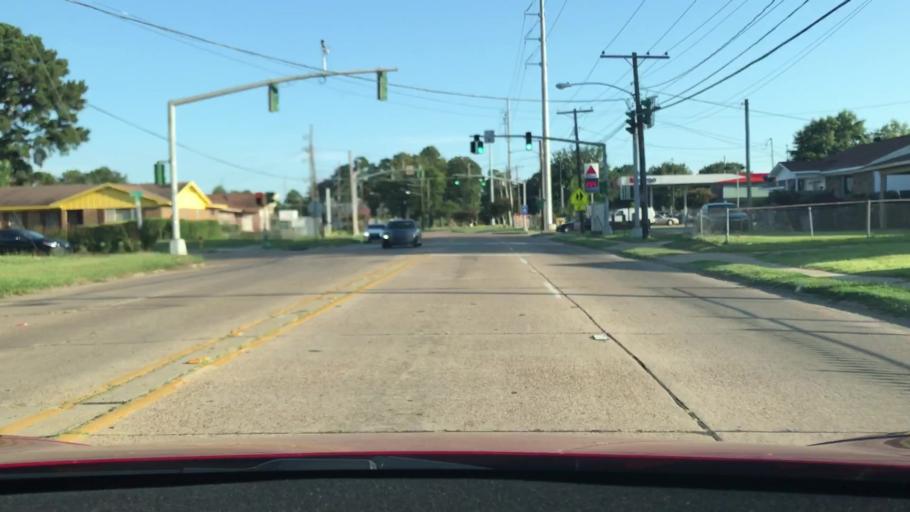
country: US
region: Louisiana
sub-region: Bossier Parish
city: Bossier City
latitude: 32.4336
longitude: -93.7460
